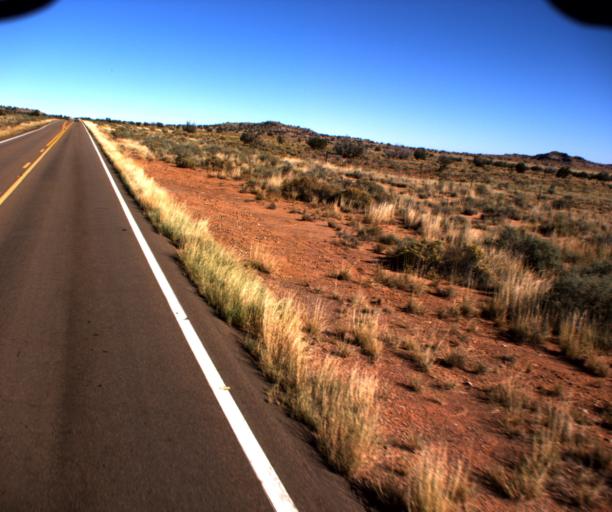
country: US
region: Arizona
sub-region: Navajo County
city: Snowflake
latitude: 34.6738
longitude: -110.1025
